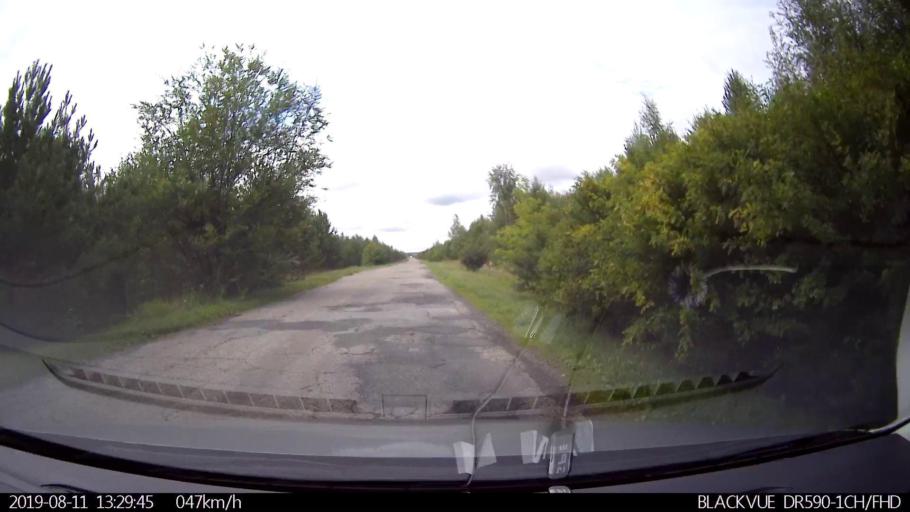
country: RU
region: Ulyanovsk
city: Ignatovka
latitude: 53.8598
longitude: 47.6110
